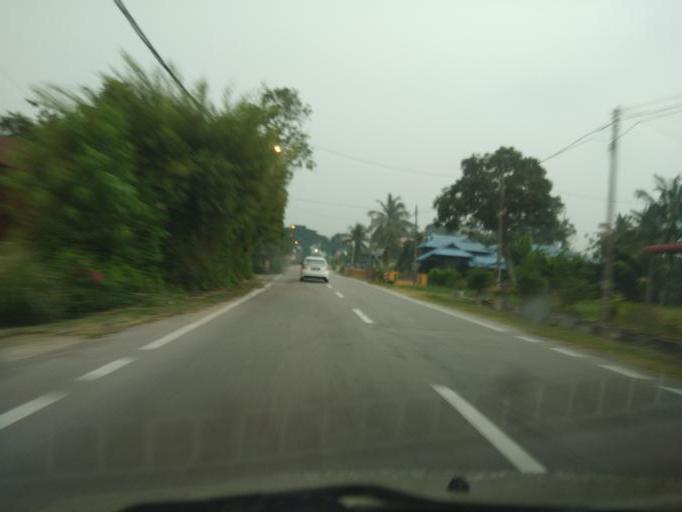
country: MY
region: Penang
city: Permatang Kuching
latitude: 5.4809
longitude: 100.4013
